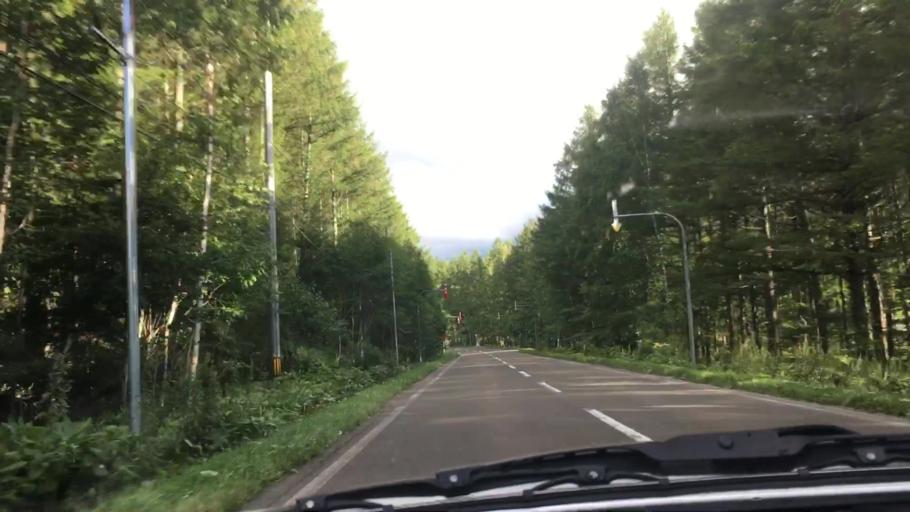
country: JP
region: Hokkaido
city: Shimo-furano
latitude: 43.1172
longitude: 142.6825
